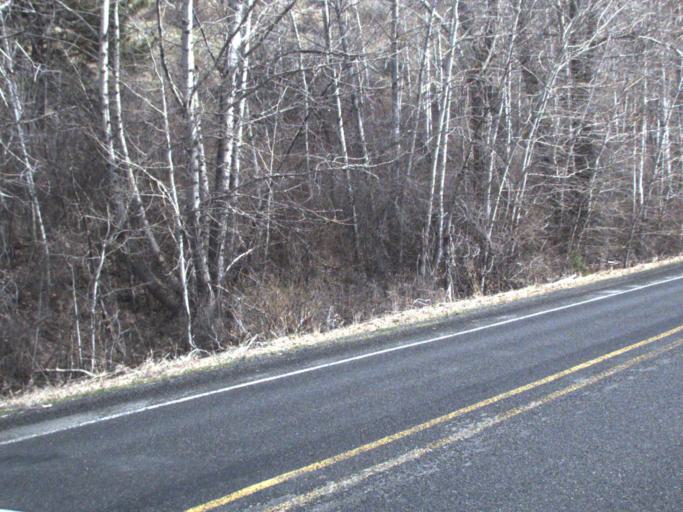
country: US
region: Washington
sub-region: Yakima County
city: Tieton
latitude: 46.8670
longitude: -120.9599
